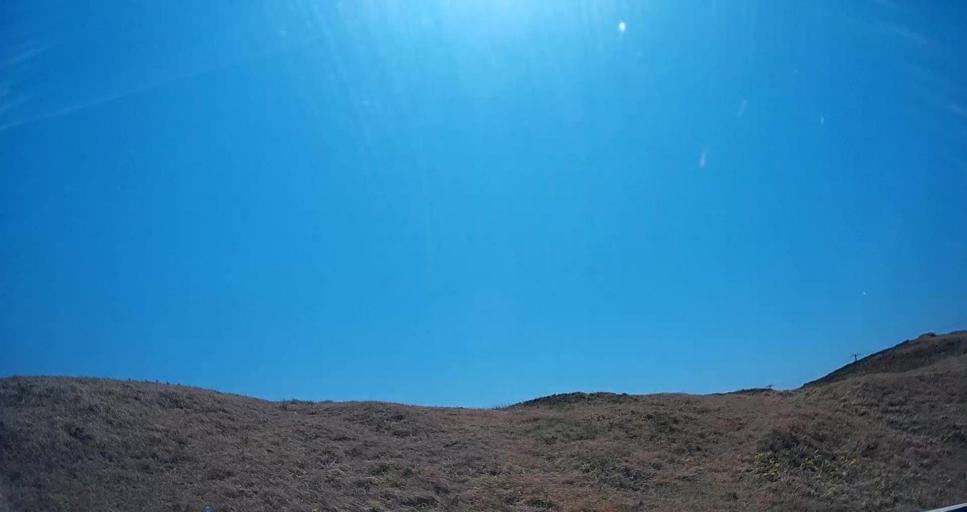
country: JP
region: Aomori
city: Mutsu
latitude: 41.4288
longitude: 141.4615
